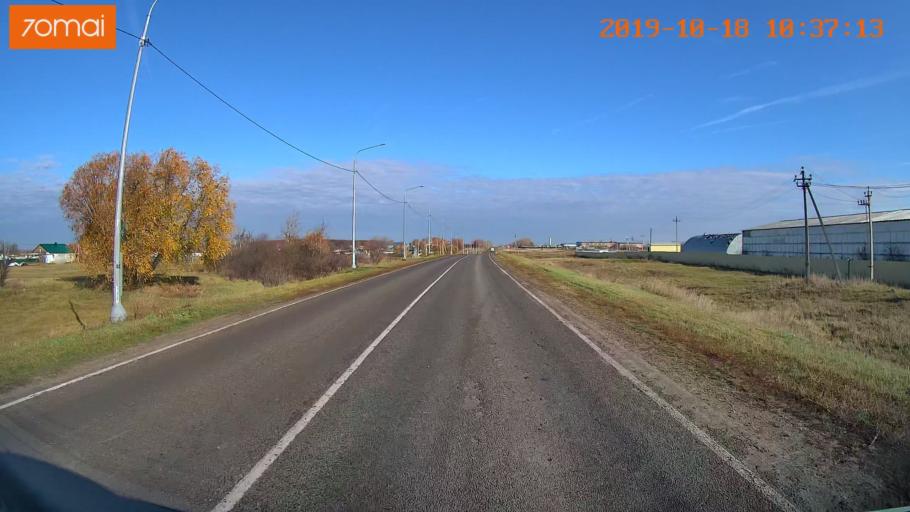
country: RU
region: Tula
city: Kurkino
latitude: 53.5595
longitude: 38.6304
